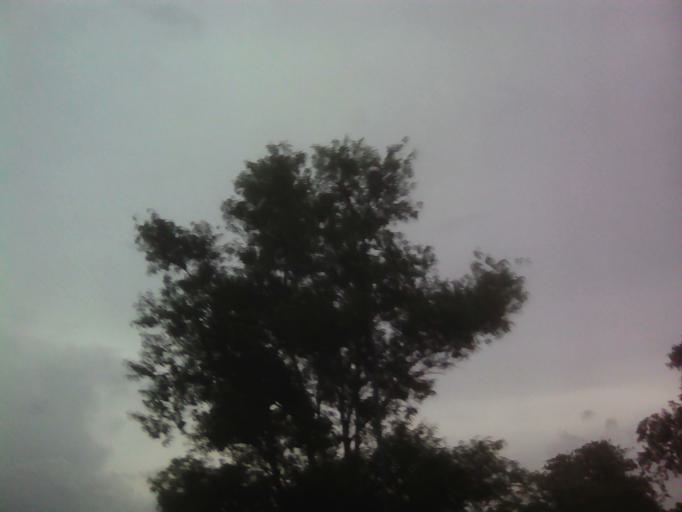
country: MY
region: Penang
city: Perai
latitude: 5.3970
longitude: 100.4199
